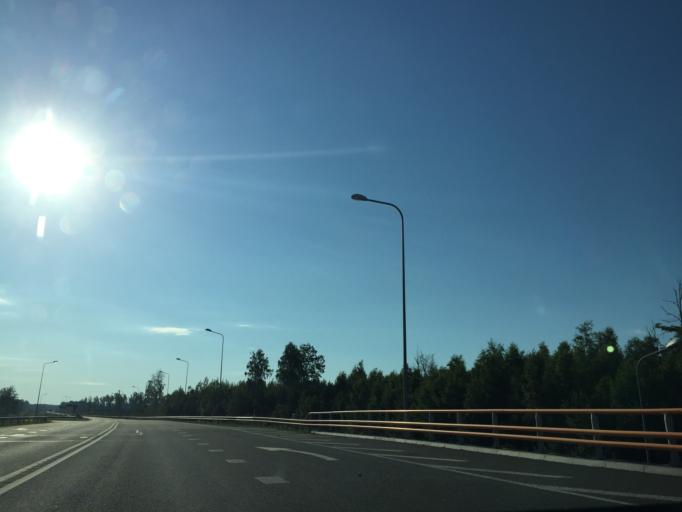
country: LV
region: Koknese
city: Koknese
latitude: 56.6668
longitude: 25.4206
